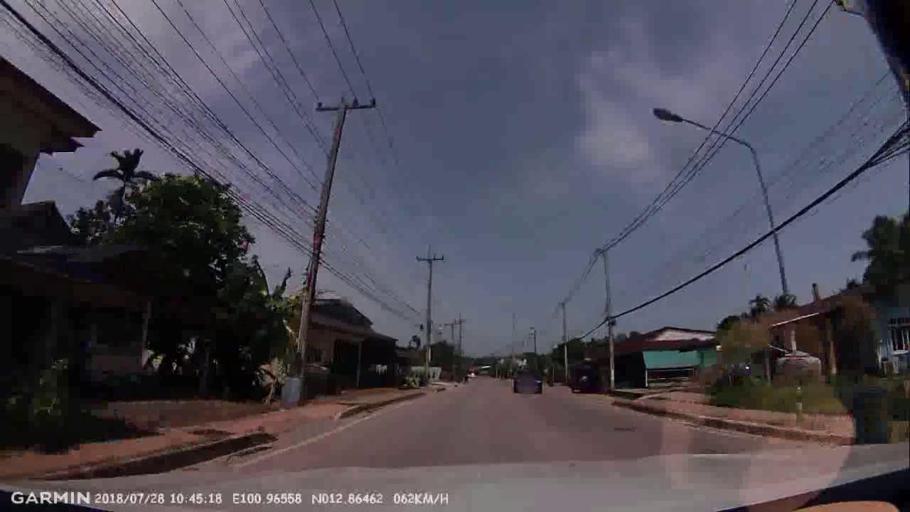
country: TH
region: Chon Buri
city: Phatthaya
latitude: 12.8646
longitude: 100.9655
